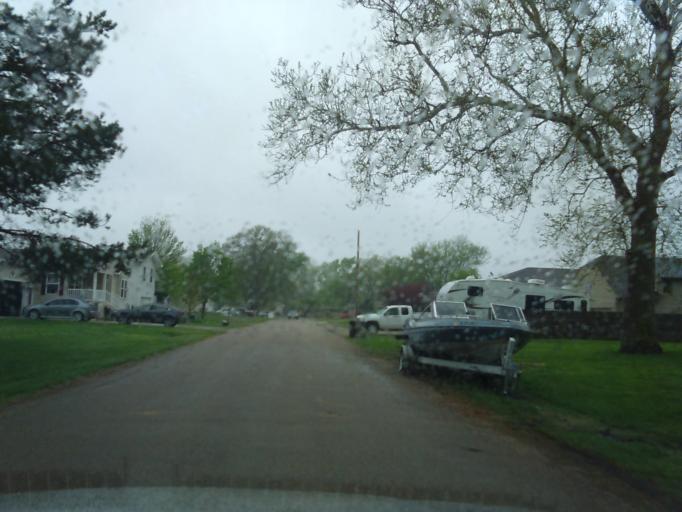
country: US
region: Nebraska
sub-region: Madison County
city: Battle Creek
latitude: 41.9985
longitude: -97.6042
